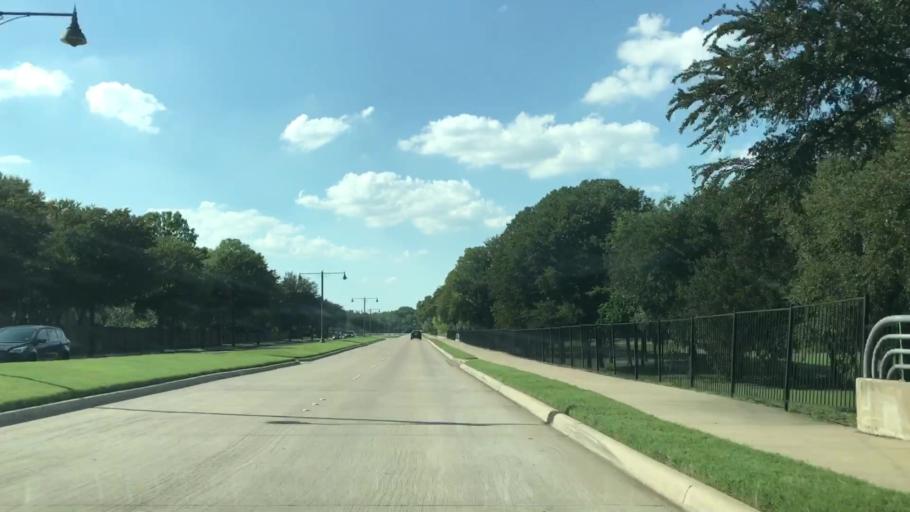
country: US
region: Texas
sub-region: Tarrant County
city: Keller
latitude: 32.9241
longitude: -97.2159
